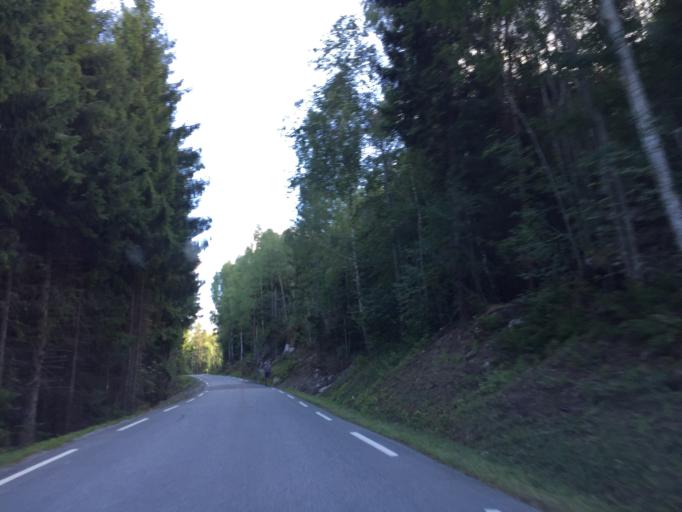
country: NO
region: Buskerud
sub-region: Ovre Eiker
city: Hokksund
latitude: 59.6509
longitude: 9.9168
